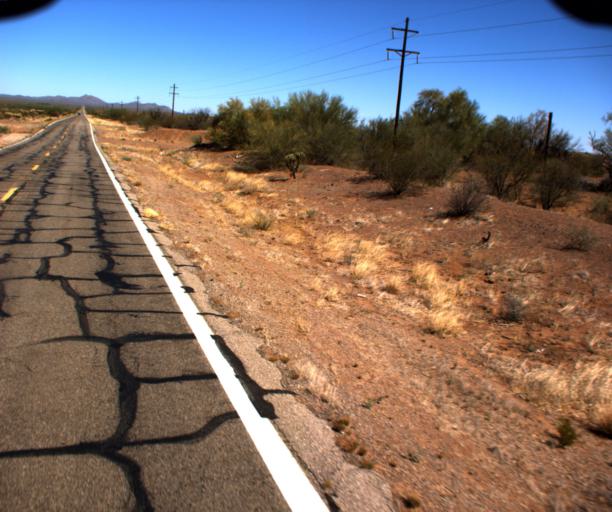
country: US
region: Arizona
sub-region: Pima County
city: Sells
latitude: 32.0794
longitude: -112.0489
